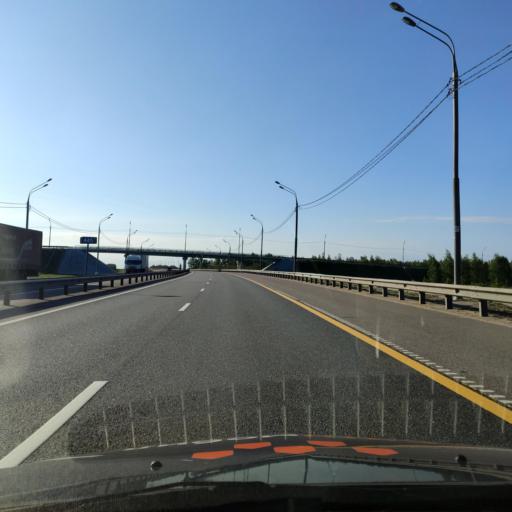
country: RU
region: Lipetsk
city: Khlevnoye
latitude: 52.2394
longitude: 39.0710
